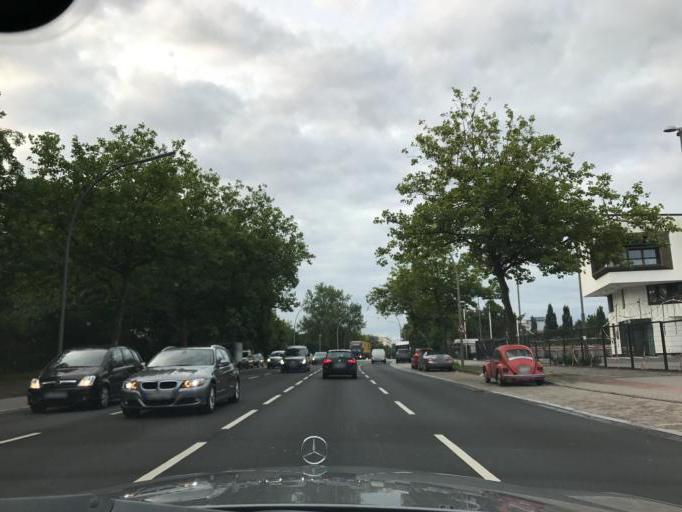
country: DE
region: Hamburg
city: Marienthal
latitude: 53.5634
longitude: 10.0789
